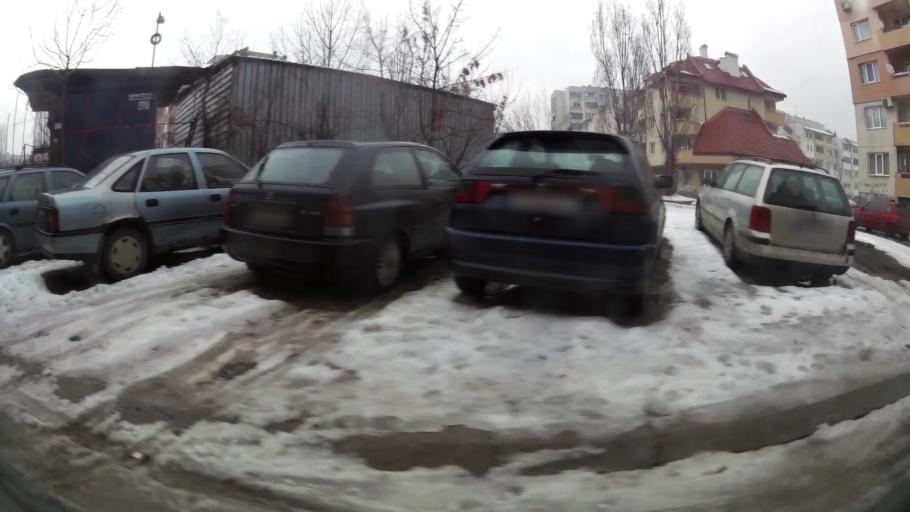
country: BG
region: Sofia-Capital
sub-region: Stolichna Obshtina
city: Sofia
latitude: 42.6826
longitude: 23.2473
